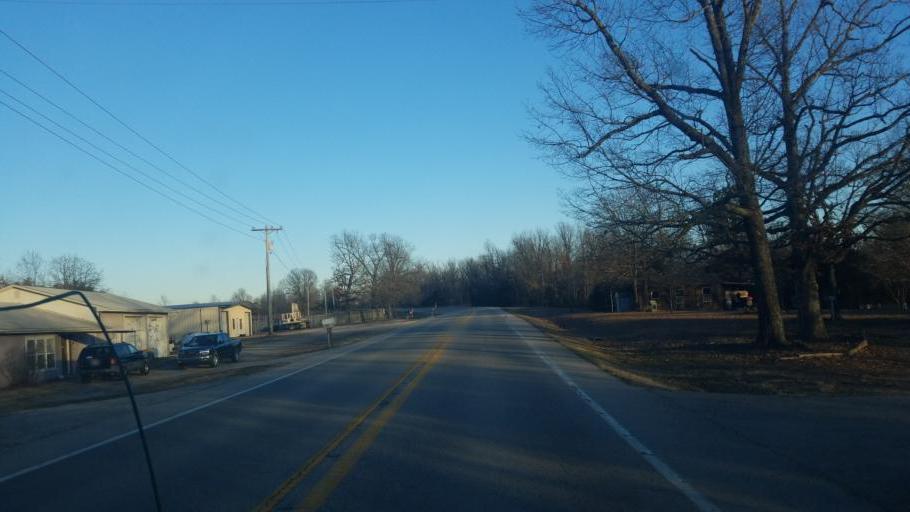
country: US
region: Arkansas
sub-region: Baxter County
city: Mountain Home
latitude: 36.3847
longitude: -92.1614
